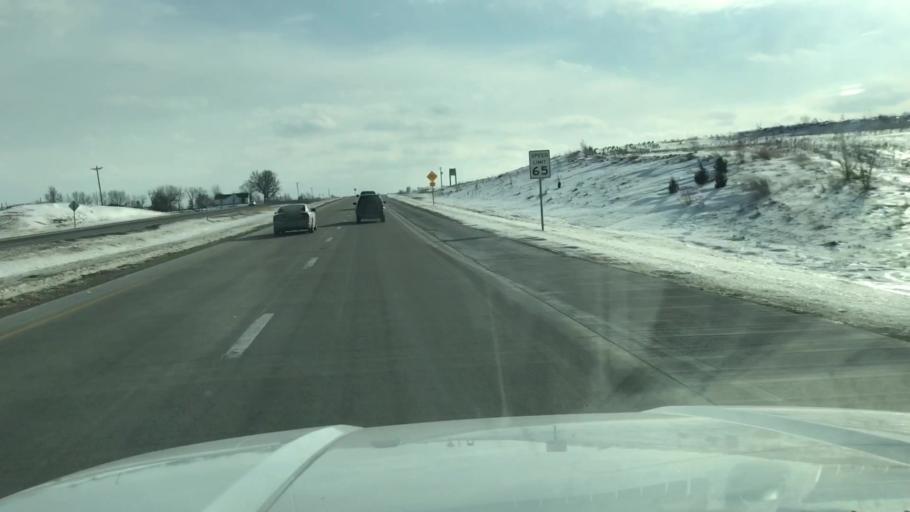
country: US
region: Missouri
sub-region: Nodaway County
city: Maryville
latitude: 40.3042
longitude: -94.8749
